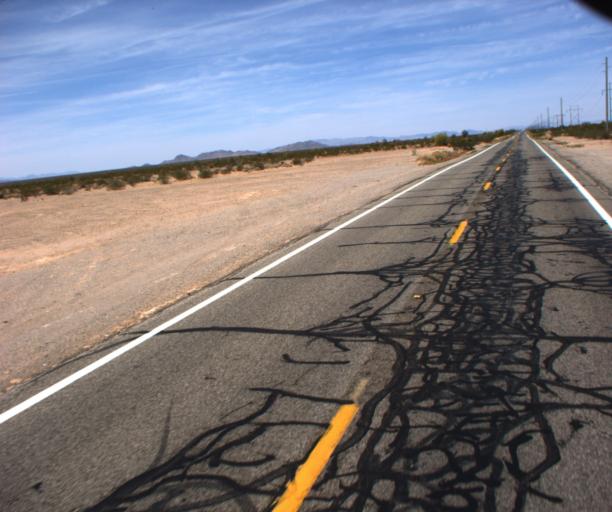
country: US
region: Arizona
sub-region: La Paz County
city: Quartzsite
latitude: 33.8312
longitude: -114.2170
